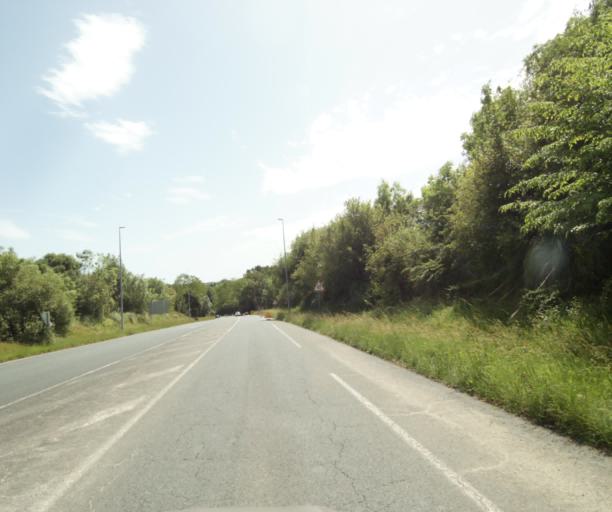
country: FR
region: Aquitaine
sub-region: Departement des Pyrenees-Atlantiques
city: Bayonne
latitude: 43.4784
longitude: -1.4551
